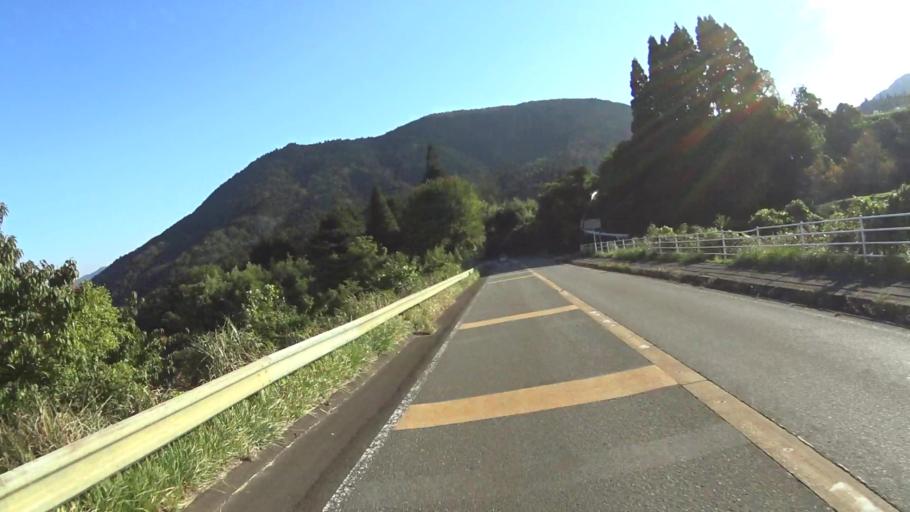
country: JP
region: Kyoto
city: Fukuchiyama
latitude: 35.4023
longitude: 135.0821
